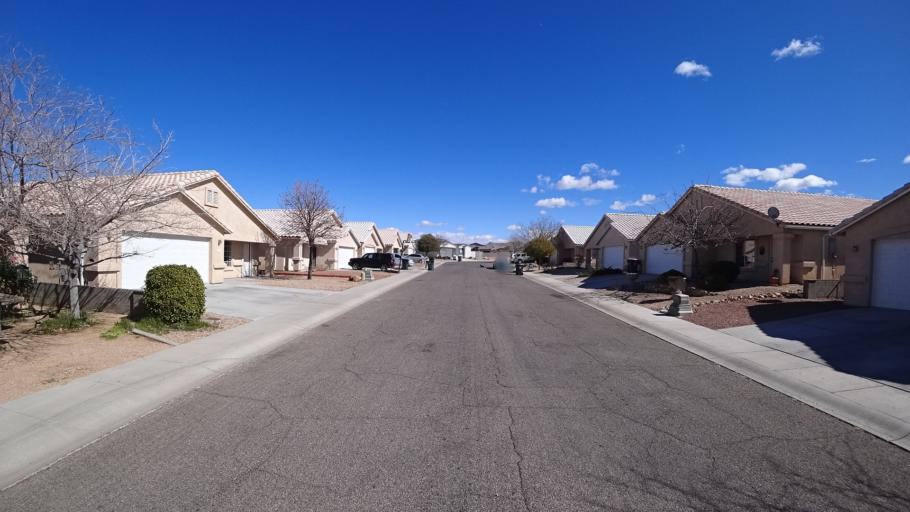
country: US
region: Arizona
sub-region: Mohave County
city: Kingman
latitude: 35.1895
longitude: -114.0084
